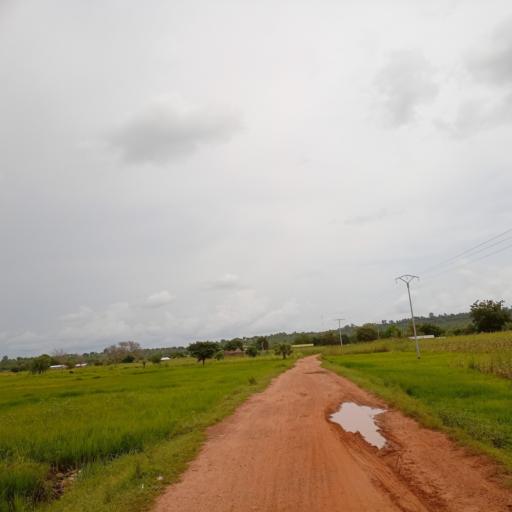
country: TG
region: Savanes
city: Dapaong
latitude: 10.8055
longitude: 0.0286
